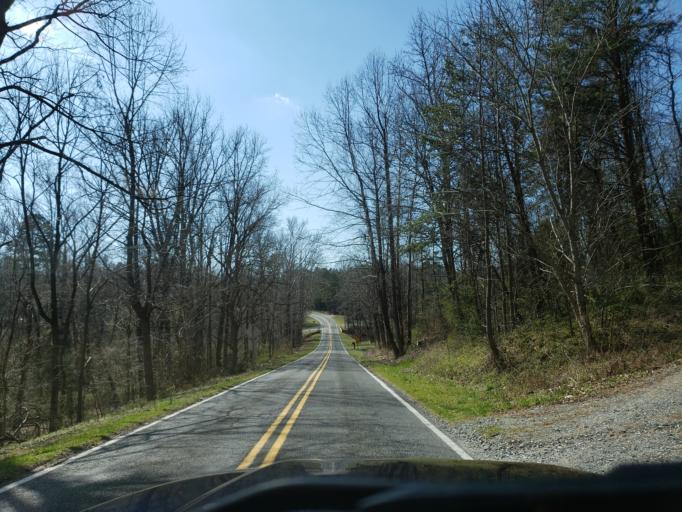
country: US
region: North Carolina
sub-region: Cleveland County
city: White Plains
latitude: 35.2268
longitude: -81.4035
